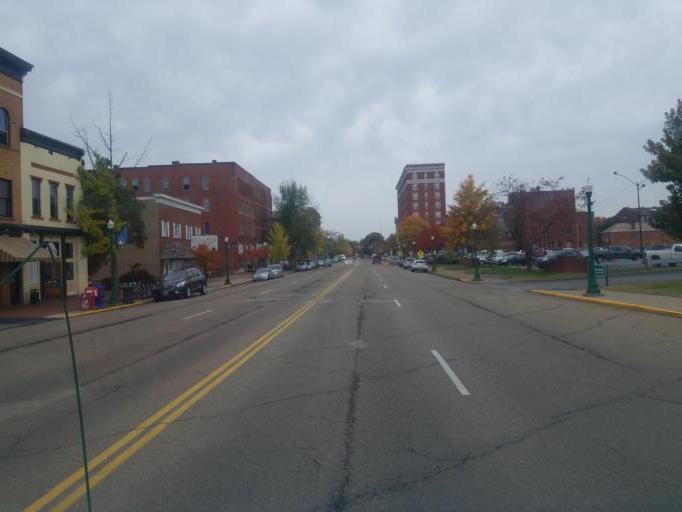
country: US
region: Ohio
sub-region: Washington County
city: Marietta
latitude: 39.4136
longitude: -81.4529
